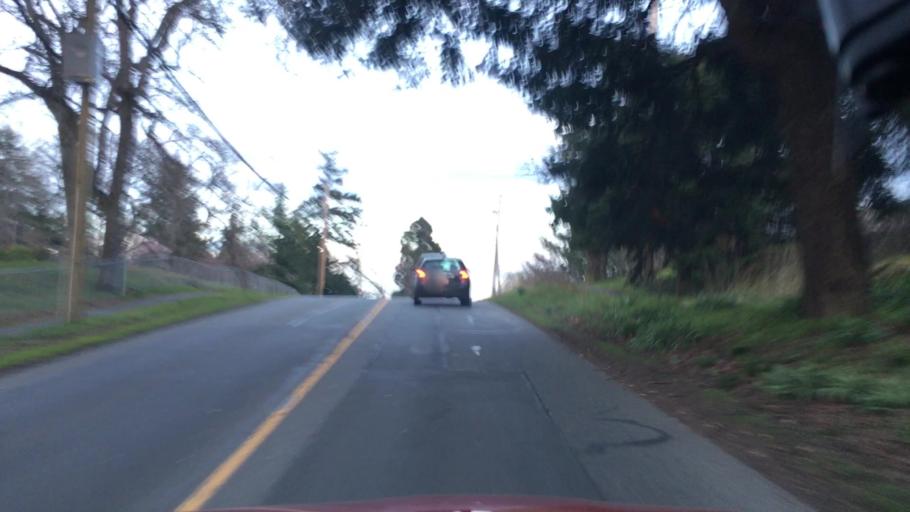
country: CA
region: British Columbia
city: Oak Bay
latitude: 48.4635
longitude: -123.3408
